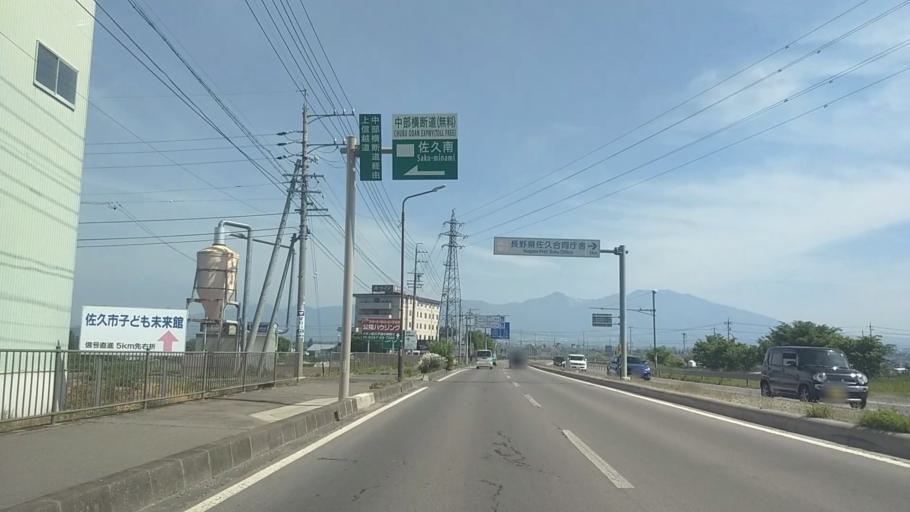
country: JP
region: Nagano
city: Saku
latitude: 36.2296
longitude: 138.4562
